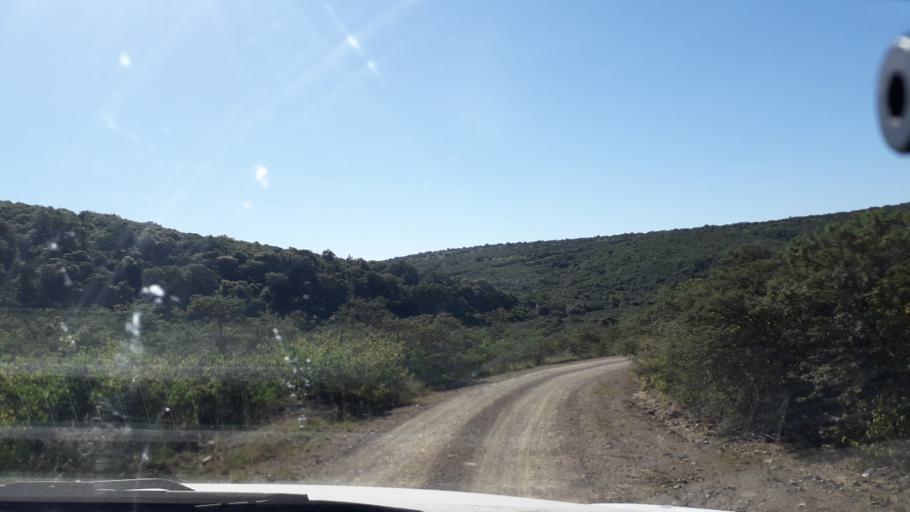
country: ZA
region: Eastern Cape
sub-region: Amathole District Municipality
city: Komga
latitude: -32.7701
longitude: 27.9604
